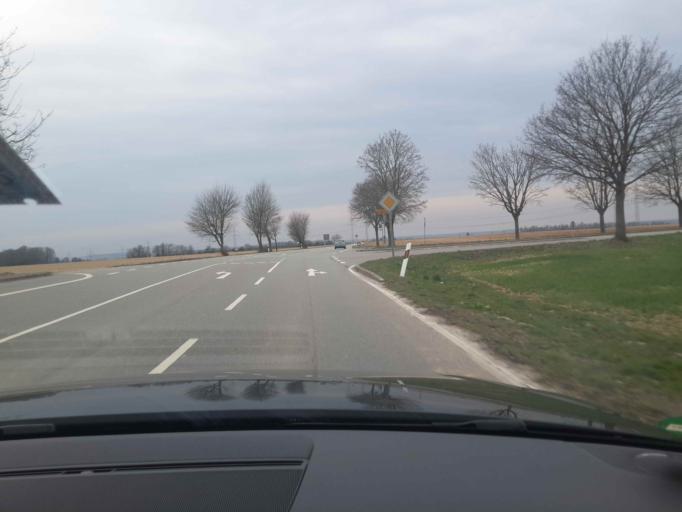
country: DE
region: Baden-Wuerttemberg
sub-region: Regierungsbezirk Stuttgart
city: Neuenstadt am Kocher
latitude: 49.2378
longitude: 9.2936
